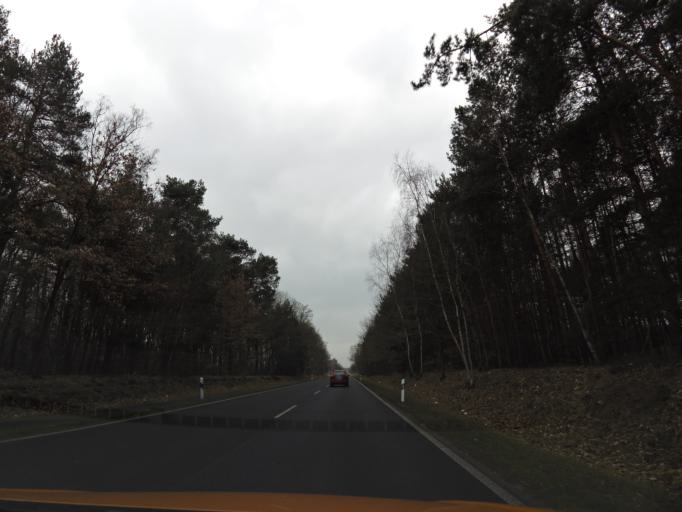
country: DE
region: Berlin
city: Kladow
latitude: 52.4922
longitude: 13.1202
